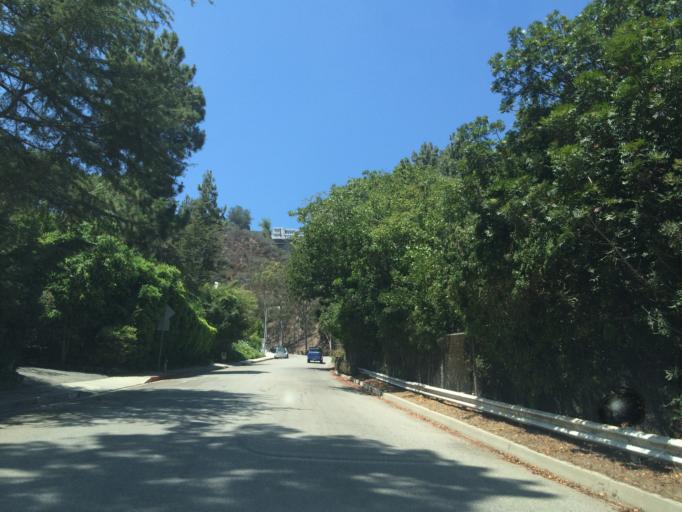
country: US
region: California
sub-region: Los Angeles County
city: Sherman Oaks
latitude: 34.1052
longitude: -118.4570
